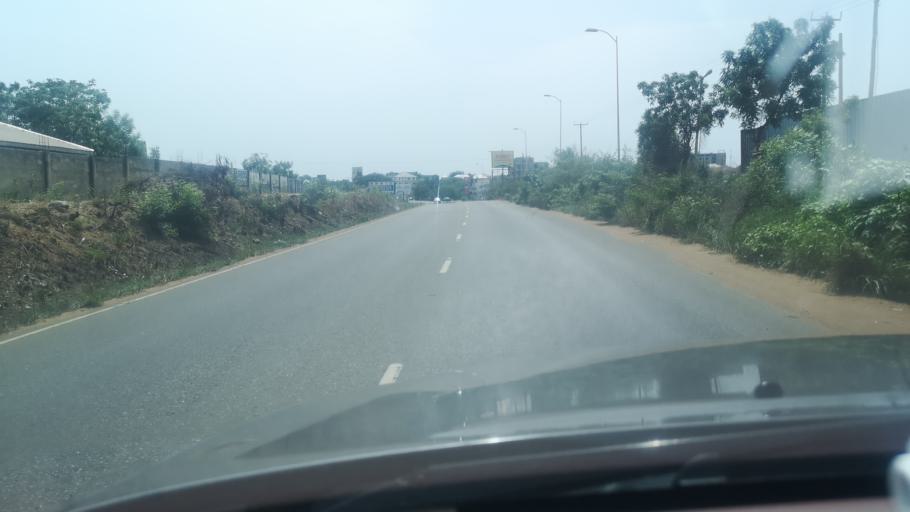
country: GH
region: Greater Accra
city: Nungua
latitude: 5.6159
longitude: -0.0642
